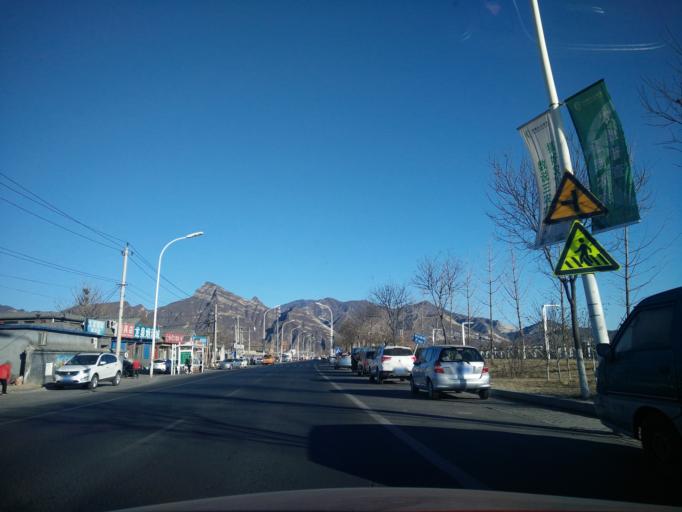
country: CN
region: Beijing
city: Junzhuang
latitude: 39.9817
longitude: 116.0821
